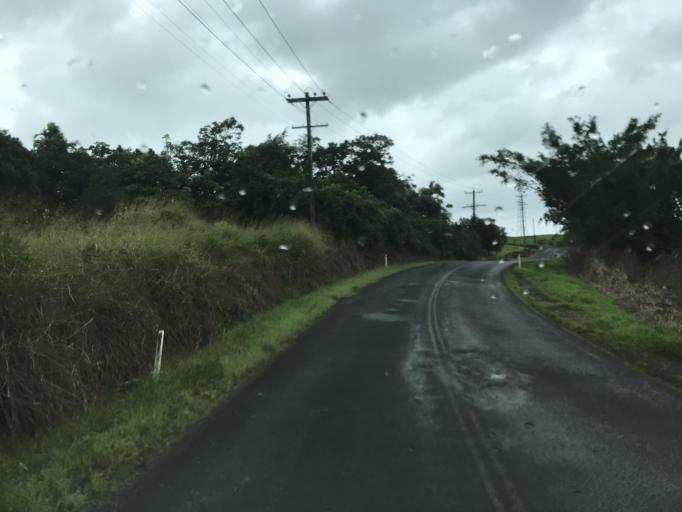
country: AU
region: Queensland
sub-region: Cassowary Coast
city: Innisfail
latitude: -17.5158
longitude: 145.9753
